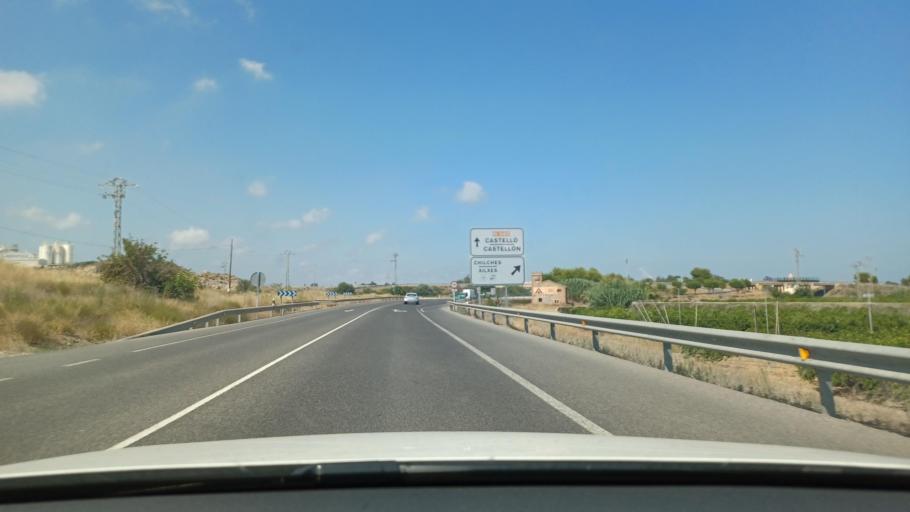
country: ES
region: Valencia
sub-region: Provincia de Castello
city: Chilches
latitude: 39.7778
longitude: -0.1968
